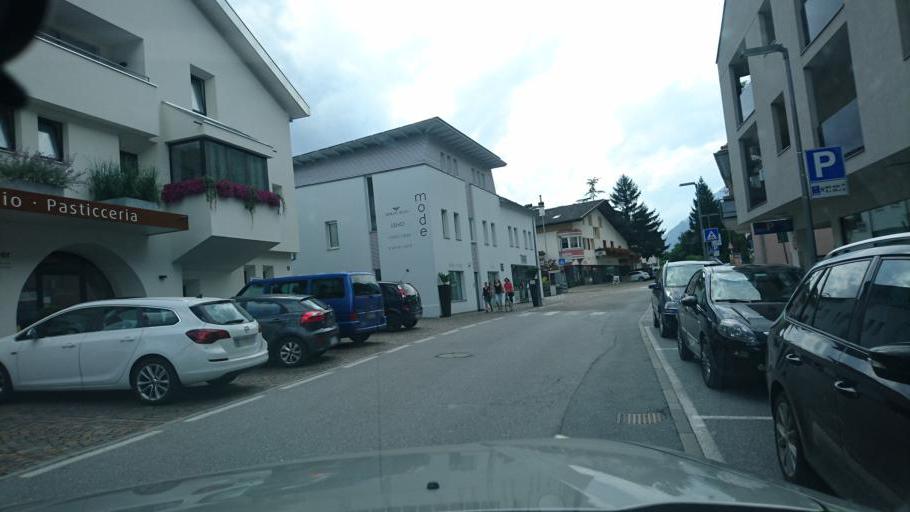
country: IT
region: Trentino-Alto Adige
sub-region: Bolzano
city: Naturno
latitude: 46.6496
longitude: 11.0024
